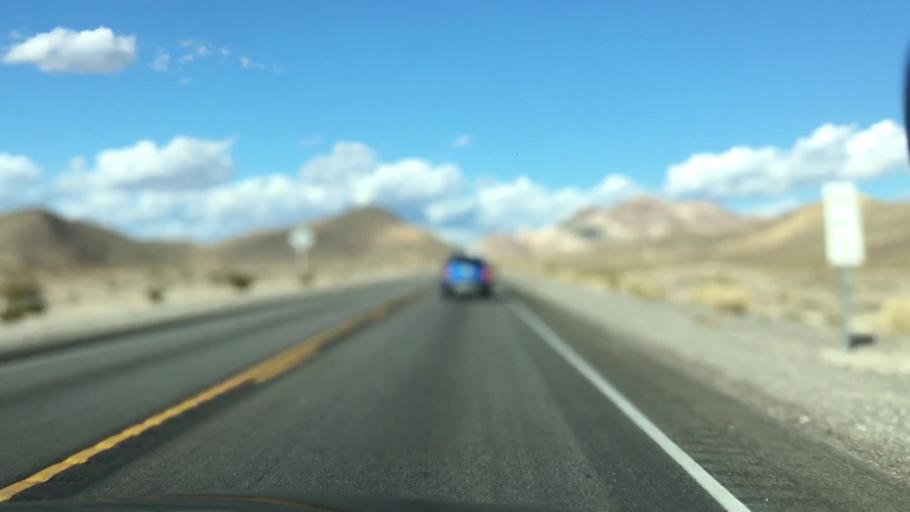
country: US
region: Nevada
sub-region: Nye County
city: Beatty
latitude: 36.8707
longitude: -116.7553
